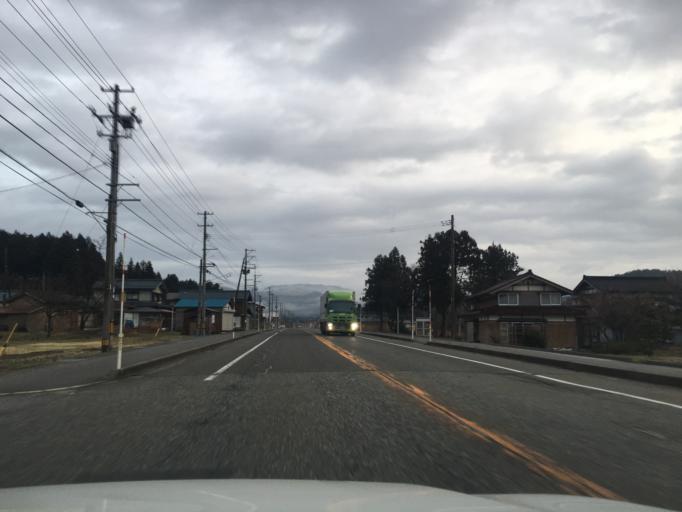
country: JP
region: Niigata
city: Murakami
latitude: 38.3150
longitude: 139.5492
